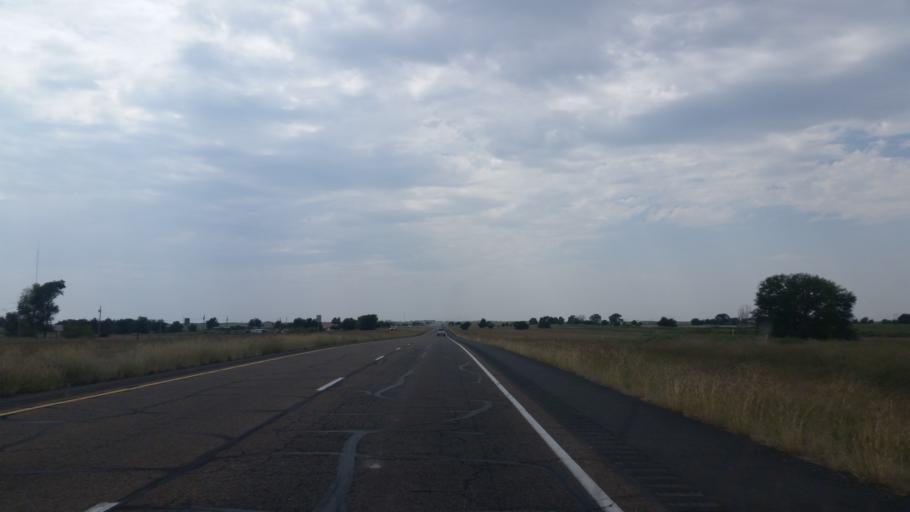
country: US
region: New Mexico
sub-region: Roosevelt County
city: Portales
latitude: 34.2491
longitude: -103.2533
